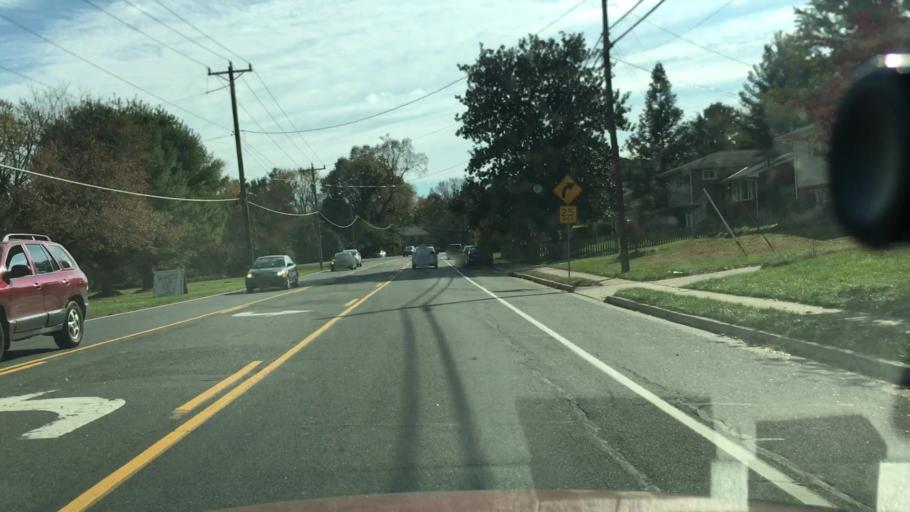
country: US
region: Virginia
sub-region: Fairfax County
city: Pimmit Hills
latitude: 38.9203
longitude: -77.1901
